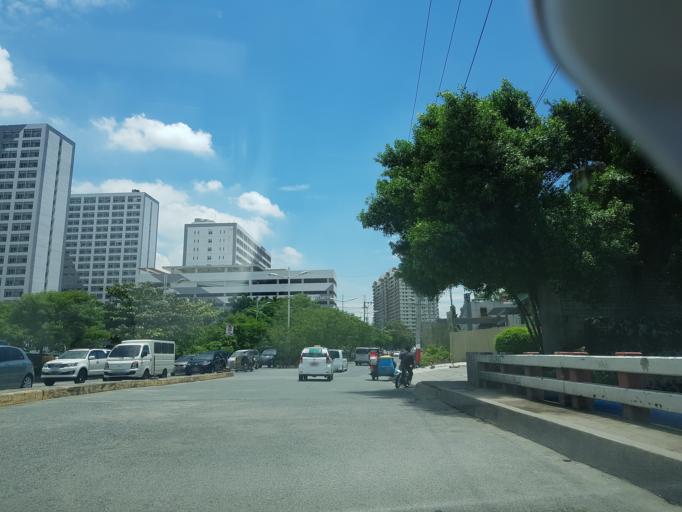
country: PH
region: Calabarzon
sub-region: Province of Rizal
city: Pateros
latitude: 14.5304
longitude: 121.0595
